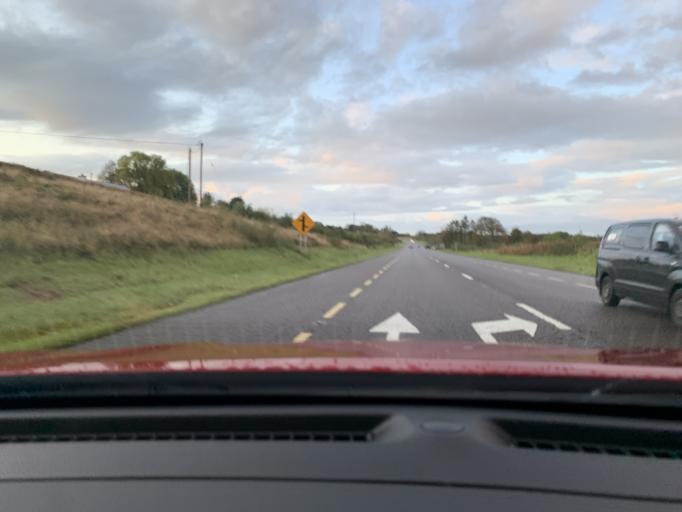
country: IE
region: Connaught
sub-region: Roscommon
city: Boyle
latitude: 54.0456
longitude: -8.3383
